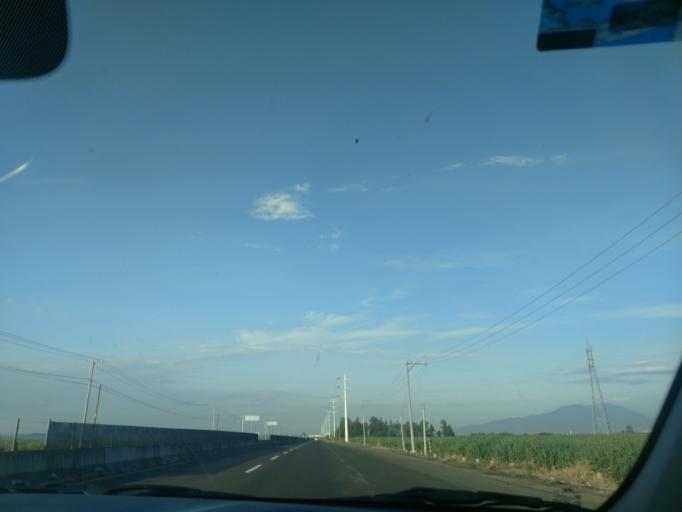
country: MX
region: Jalisco
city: El Refugio
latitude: 20.6557
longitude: -103.7367
